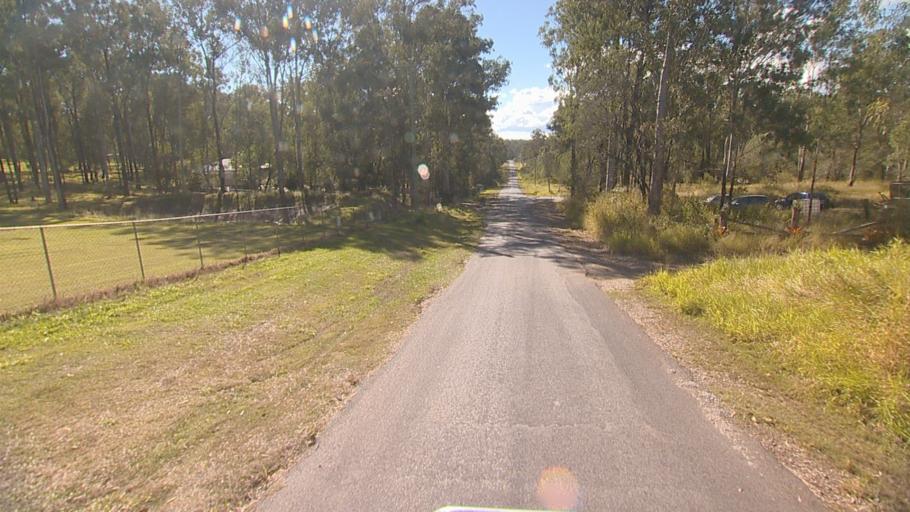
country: AU
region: Queensland
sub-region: Logan
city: Chambers Flat
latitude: -27.8101
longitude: 153.0819
